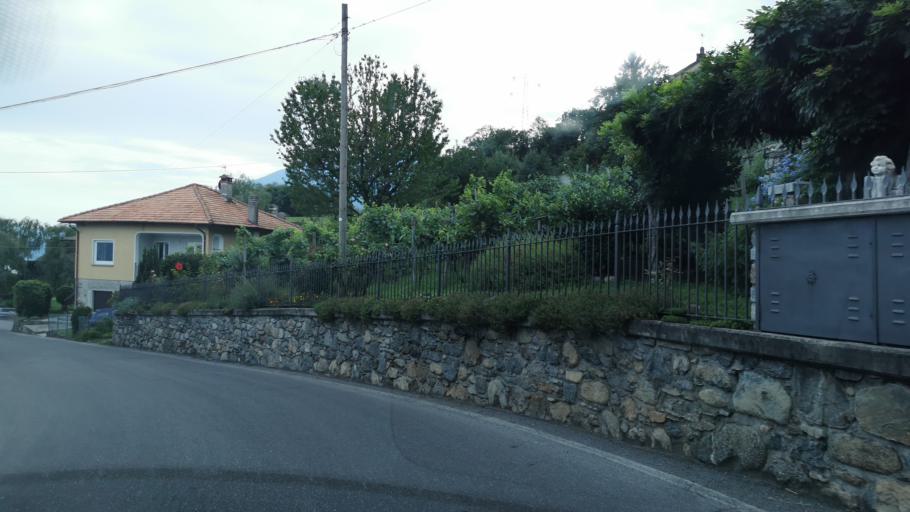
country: IT
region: Lombardy
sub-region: Provincia di Como
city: Domaso
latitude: 46.1568
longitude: 9.3314
